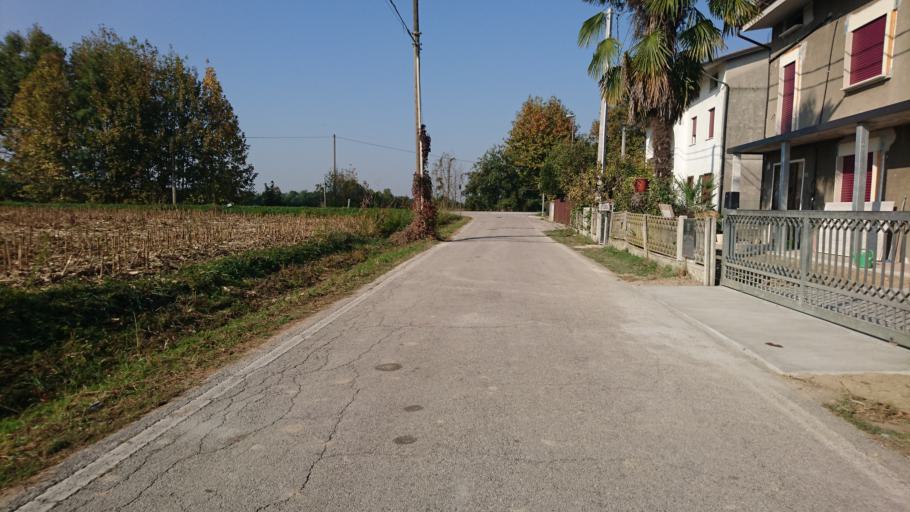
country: IT
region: Veneto
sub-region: Provincia di Padova
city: Gazzo
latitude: 45.5984
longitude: 11.6928
